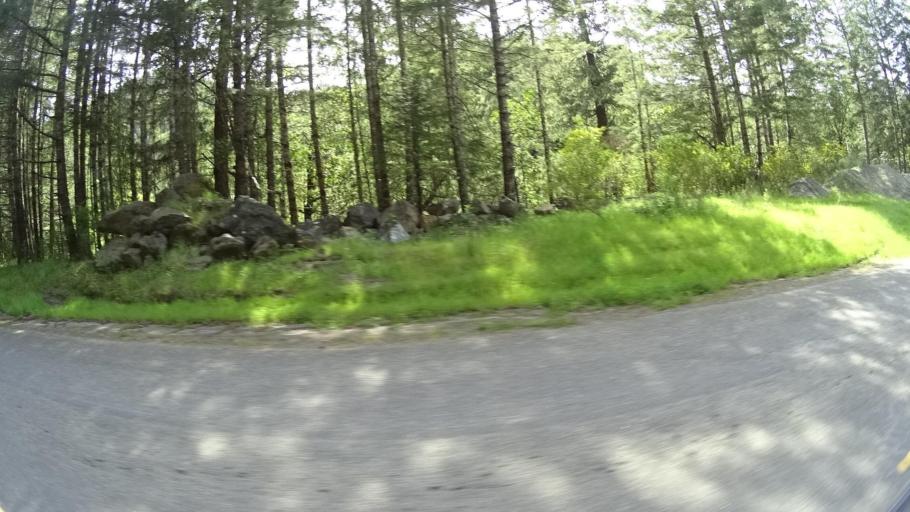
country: US
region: California
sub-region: Humboldt County
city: Rio Dell
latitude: 40.4580
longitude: -123.8042
